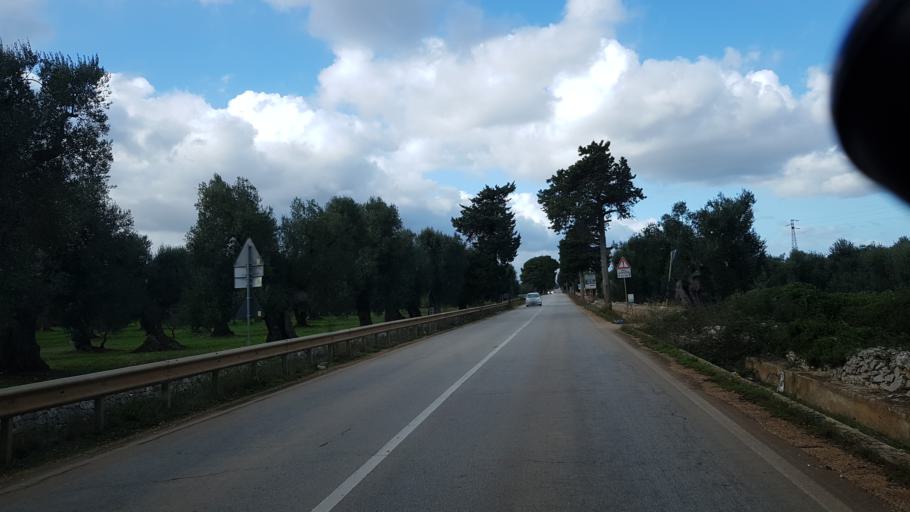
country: IT
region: Apulia
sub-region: Provincia di Brindisi
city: Montalbano
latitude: 40.7675
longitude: 17.5132
